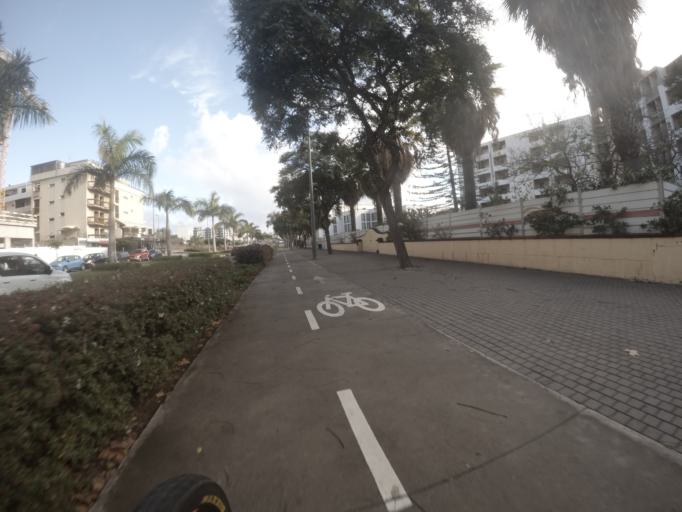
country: PT
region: Madeira
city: Camara de Lobos
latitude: 32.6395
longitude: -16.9474
